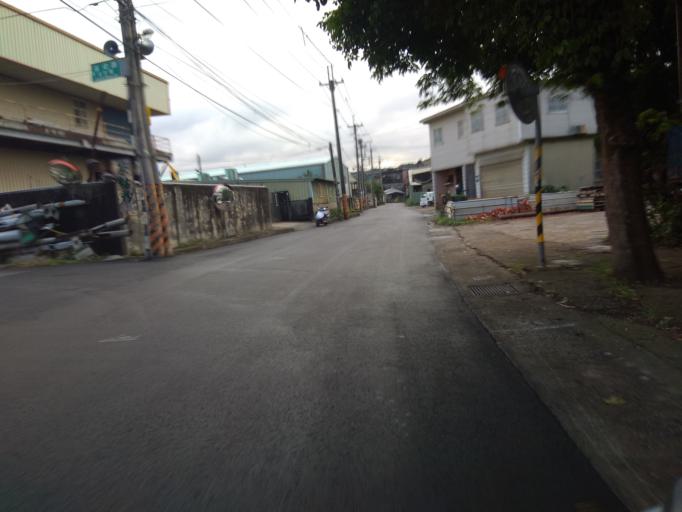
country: TW
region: Taiwan
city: Daxi
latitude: 24.9405
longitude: 121.1898
